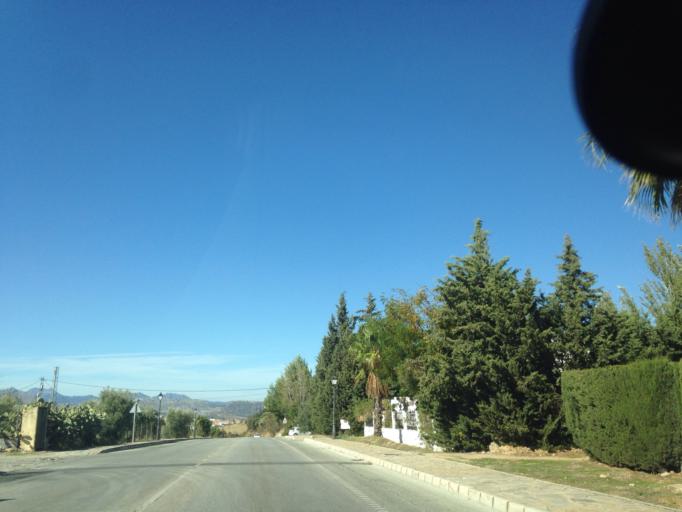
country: ES
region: Andalusia
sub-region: Provincia de Malaga
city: Ronda
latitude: 36.7282
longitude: -5.1535
